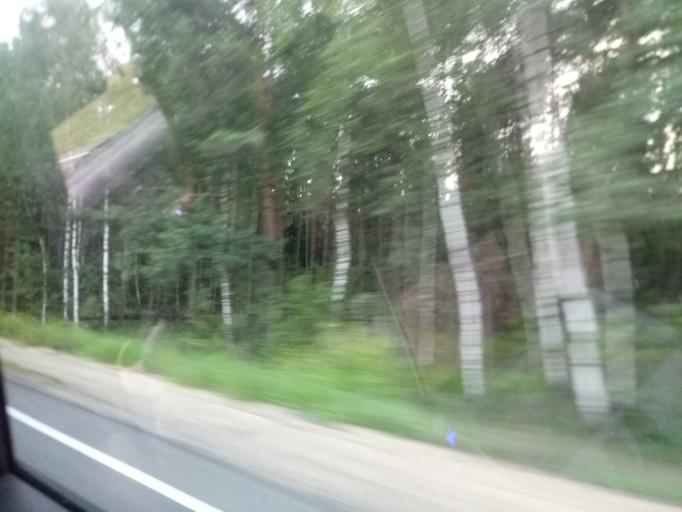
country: RU
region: Moskovskaya
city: Noginsk-9
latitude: 56.0901
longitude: 38.5798
